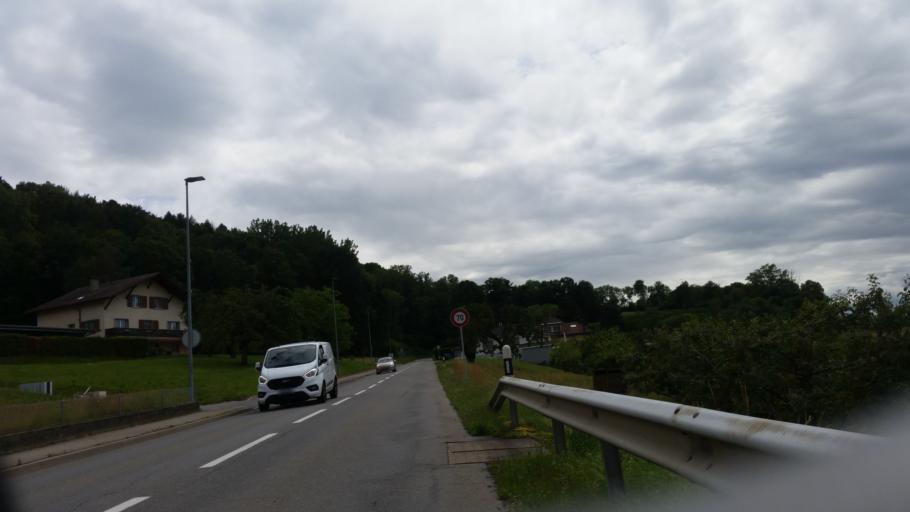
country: CH
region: Fribourg
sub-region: Broye District
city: Estavayer-le-Lac
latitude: 46.8349
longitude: 6.8180
